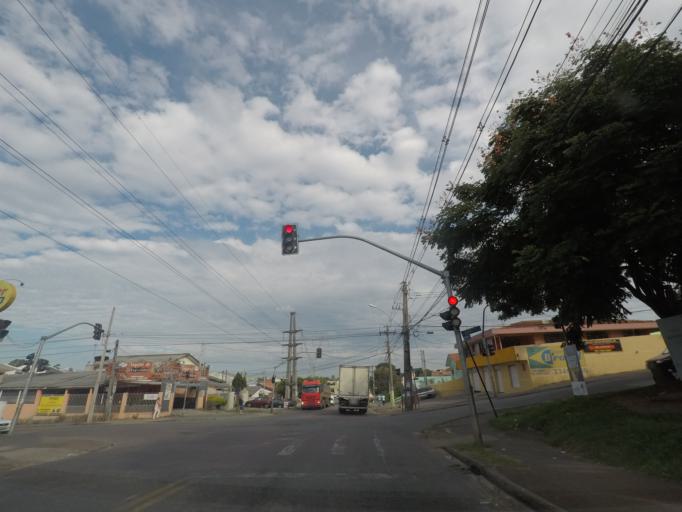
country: BR
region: Parana
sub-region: Sao Jose Dos Pinhais
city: Sao Jose dos Pinhais
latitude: -25.5507
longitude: -49.2928
